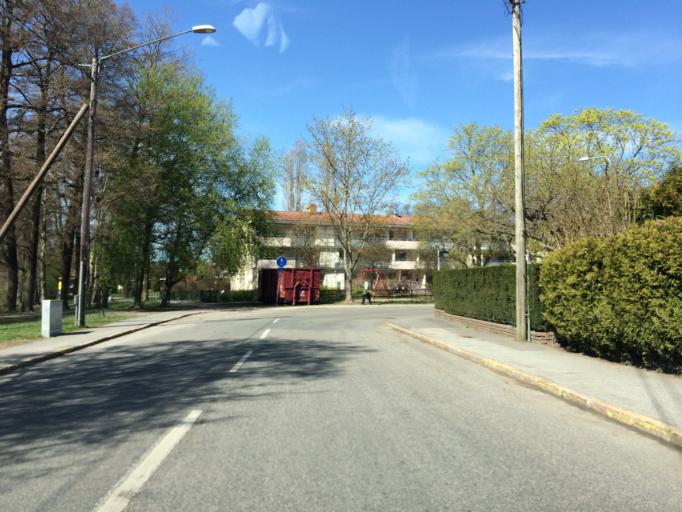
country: SE
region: Stockholm
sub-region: Huddinge Kommun
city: Huddinge
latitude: 59.2686
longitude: 17.9705
